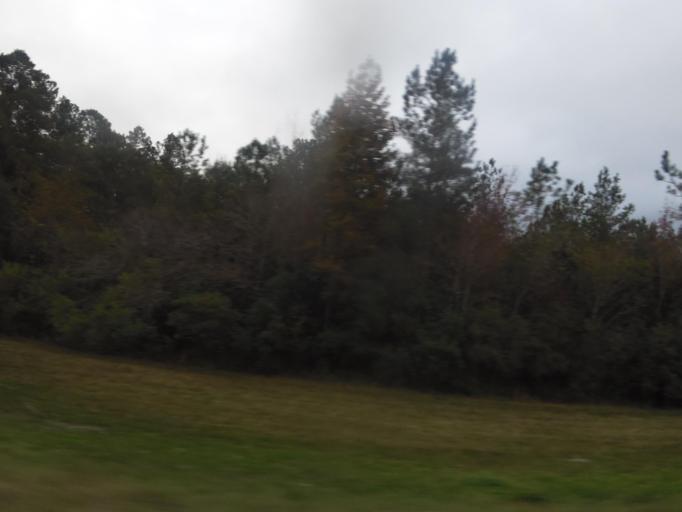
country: US
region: Georgia
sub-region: Charlton County
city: Folkston
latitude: 30.8031
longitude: -82.0286
